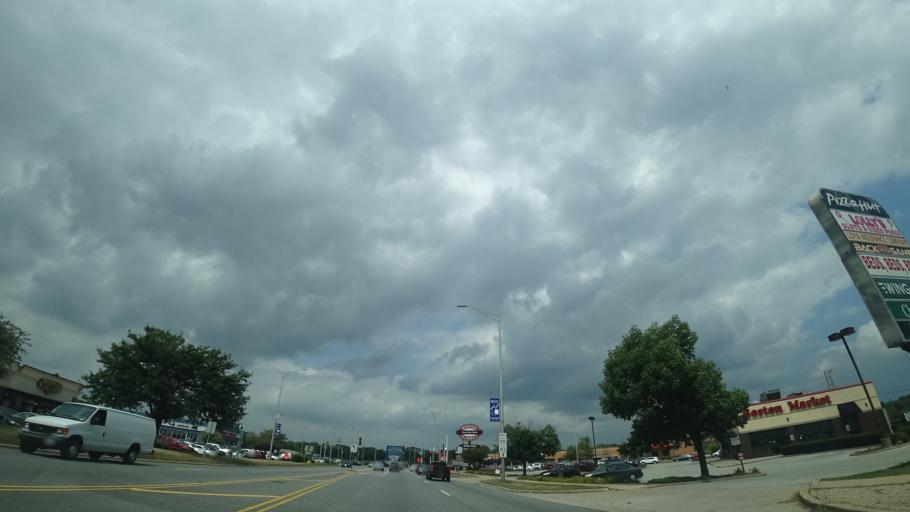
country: US
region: Illinois
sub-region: Cook County
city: Alsip
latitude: 41.6521
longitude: -87.7382
